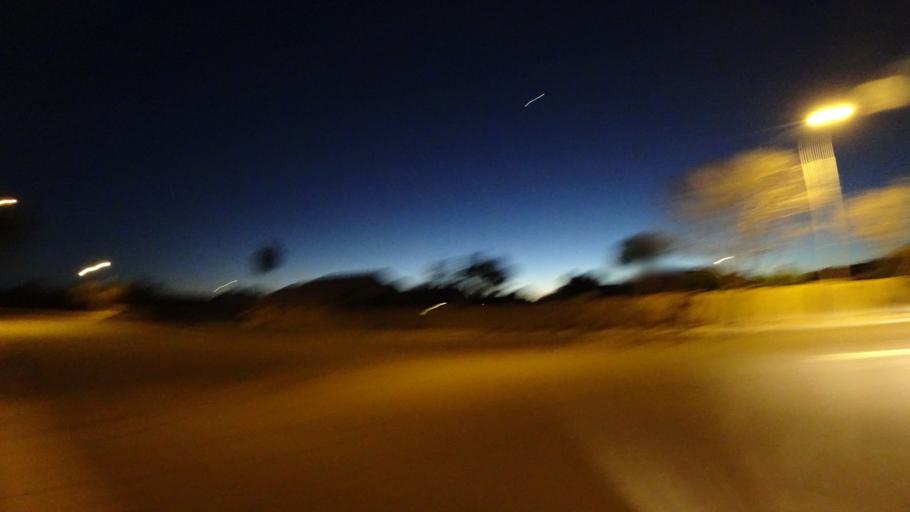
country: US
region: Arizona
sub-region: Maricopa County
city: Chandler
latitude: 33.2892
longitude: -111.8675
